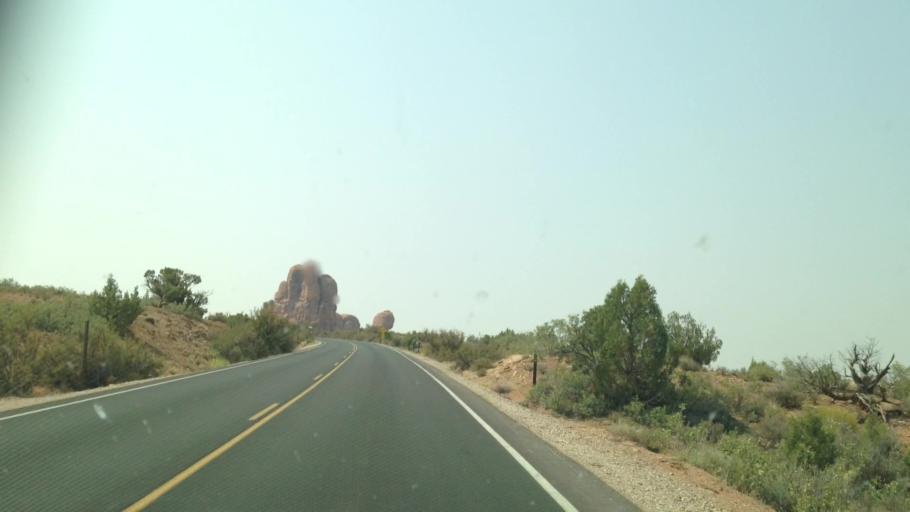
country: US
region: Utah
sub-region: Grand County
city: Moab
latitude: 38.7081
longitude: -109.5620
